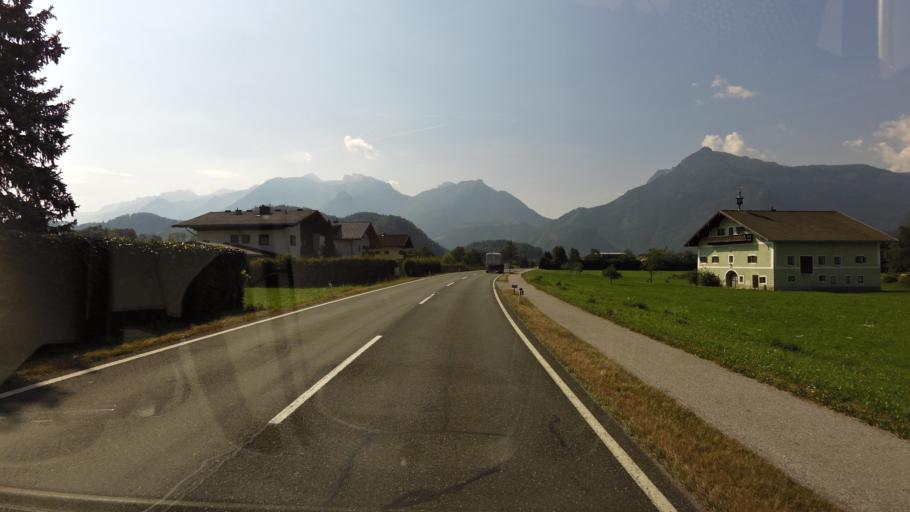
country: AT
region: Salzburg
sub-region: Politischer Bezirk Hallein
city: Golling an der Salzach
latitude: 47.6122
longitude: 13.1672
